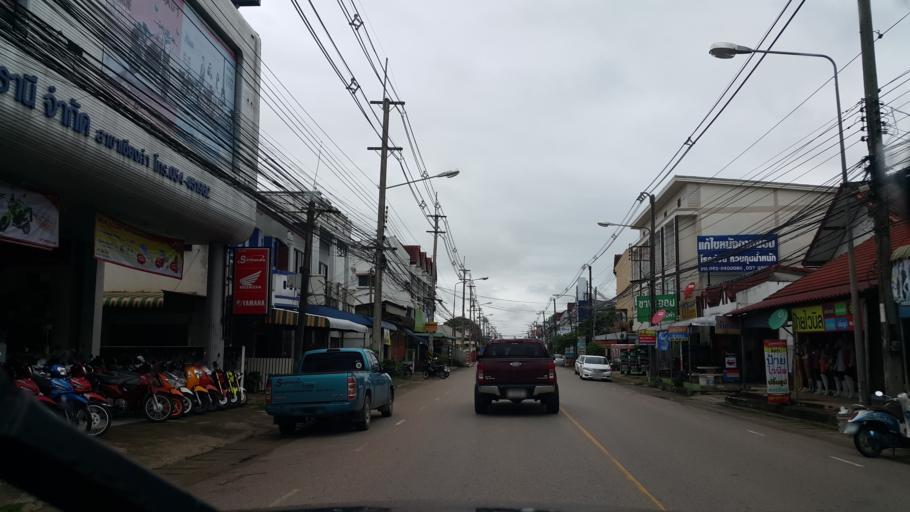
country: TH
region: Phayao
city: Chiang Kham
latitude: 19.5283
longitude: 100.3020
